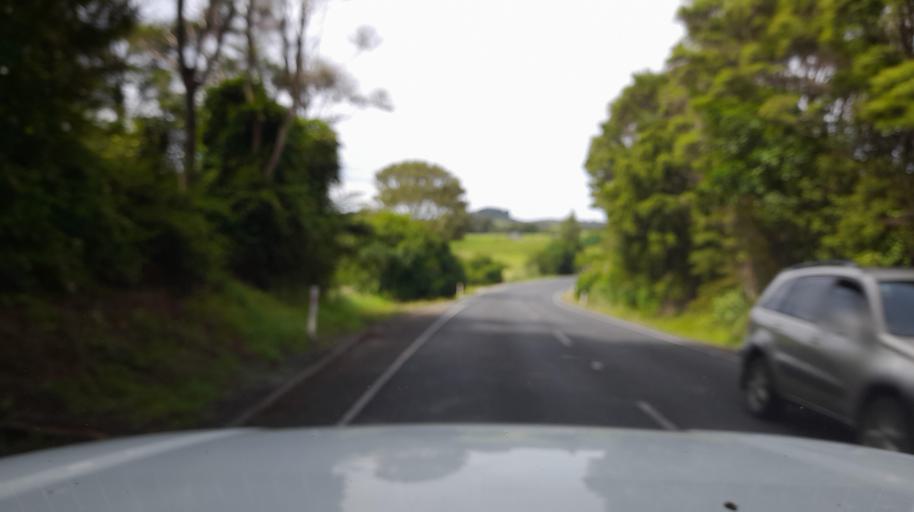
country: NZ
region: Northland
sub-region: Far North District
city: Taipa
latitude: -35.2599
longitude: 173.5278
